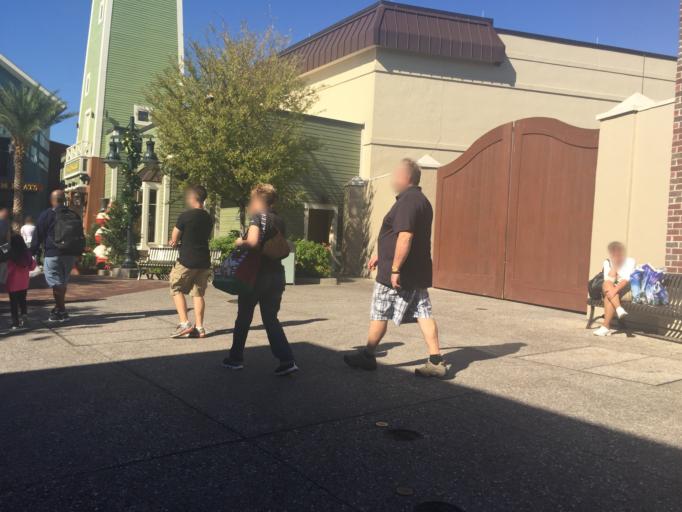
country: US
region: Florida
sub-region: Osceola County
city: Celebration
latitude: 28.3717
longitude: -81.5176
